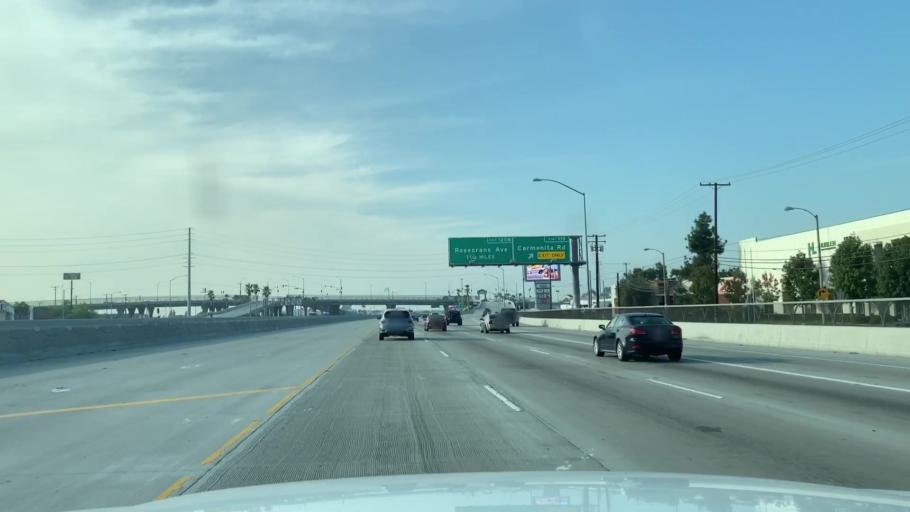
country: US
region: California
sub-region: Los Angeles County
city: Cerritos
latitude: 33.8916
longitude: -118.0427
